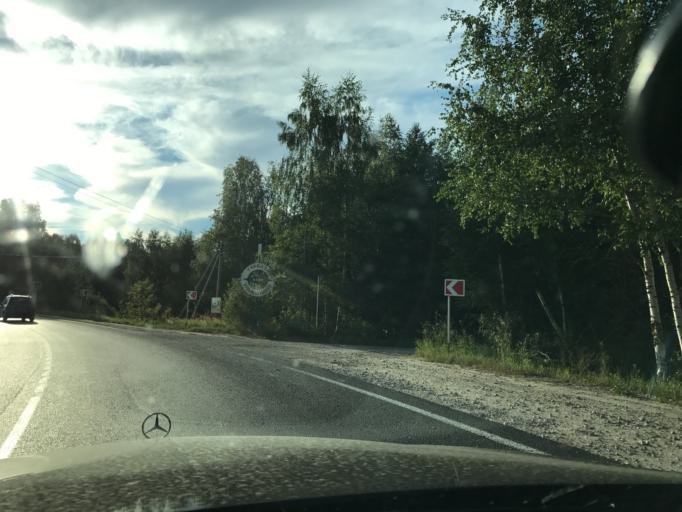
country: RU
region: Vladimir
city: Raduzhnyy
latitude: 56.0332
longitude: 40.3609
